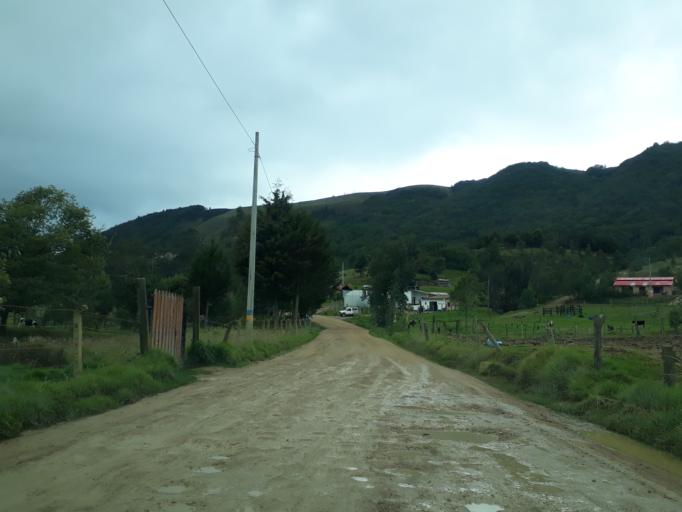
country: CO
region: Cundinamarca
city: Cucunuba
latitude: 5.2032
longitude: -73.7730
